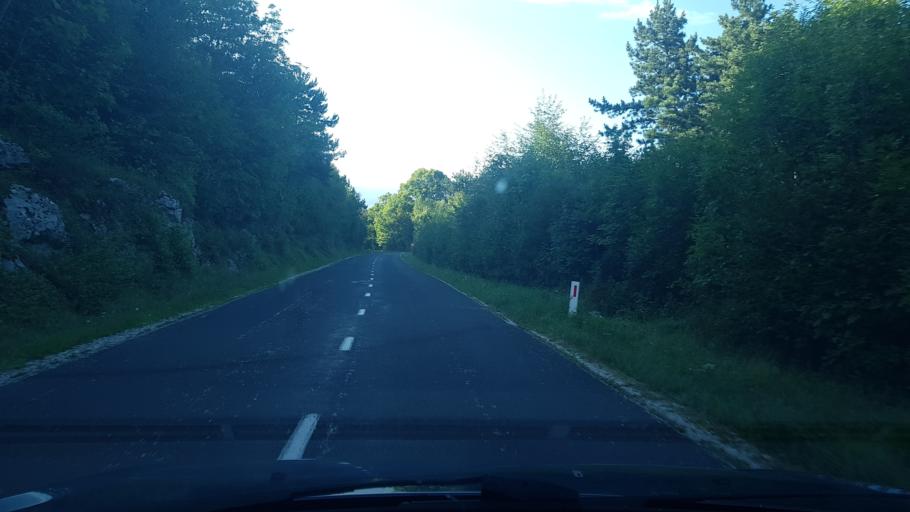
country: SI
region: Nova Gorica
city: Solkan
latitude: 46.0197
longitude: 13.6790
